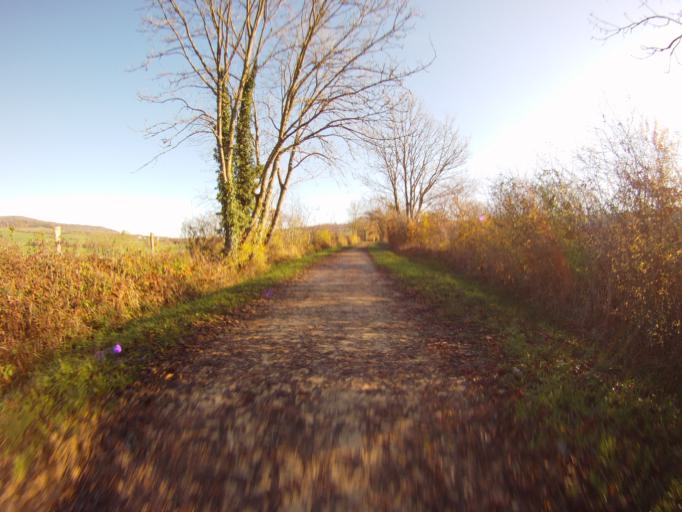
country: FR
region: Lorraine
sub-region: Departement de Meurthe-et-Moselle
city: Faulx
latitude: 48.7923
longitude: 6.2159
